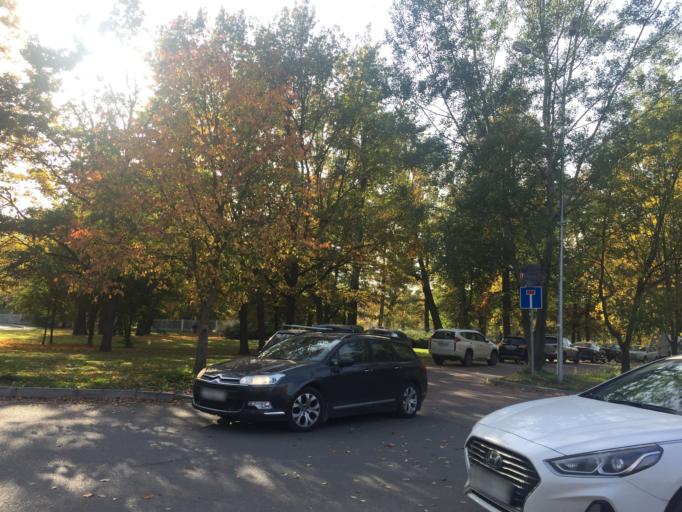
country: RU
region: St.-Petersburg
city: Pushkin
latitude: 59.7230
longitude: 30.3967
